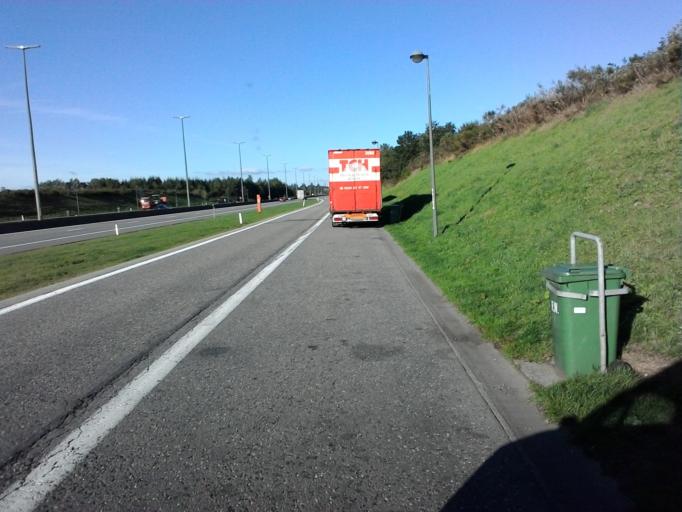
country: BE
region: Wallonia
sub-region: Province du Luxembourg
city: Bastogne
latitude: 50.0429
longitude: 5.7097
